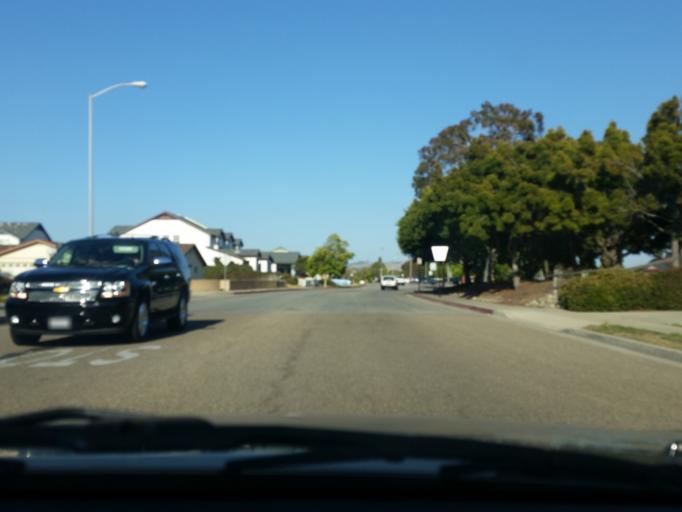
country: US
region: California
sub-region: San Luis Obispo County
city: Grover Beach
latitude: 35.1149
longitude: -120.6085
